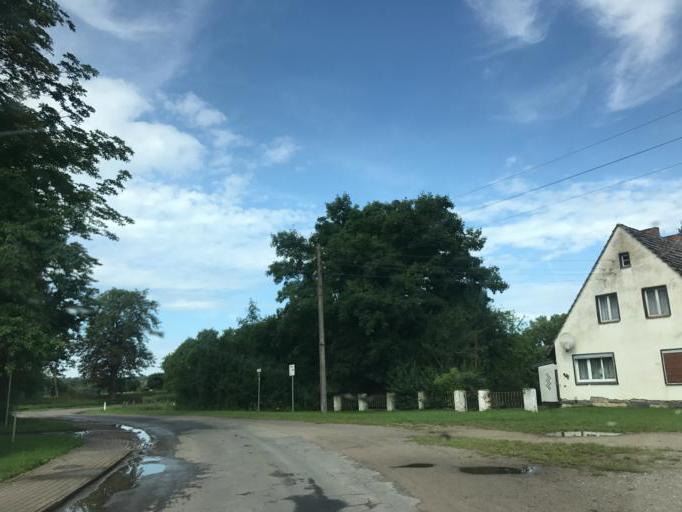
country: DE
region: Mecklenburg-Vorpommern
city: Rechlin
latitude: 53.3385
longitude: 12.8454
